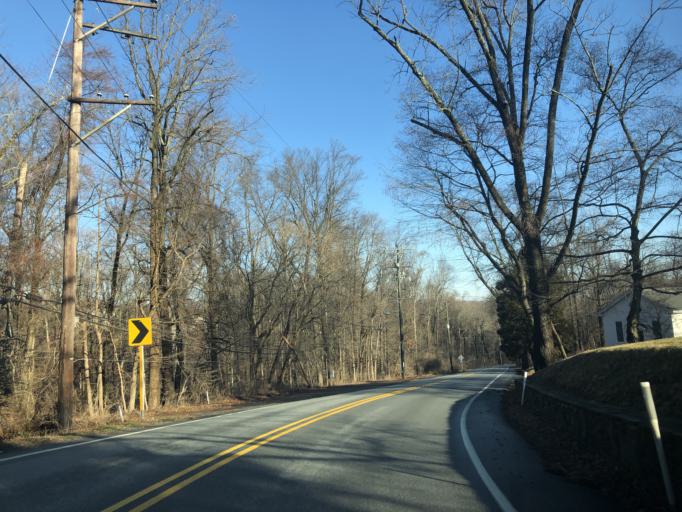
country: US
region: Pennsylvania
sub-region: Delaware County
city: Chester Heights
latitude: 39.9005
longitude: -75.4888
